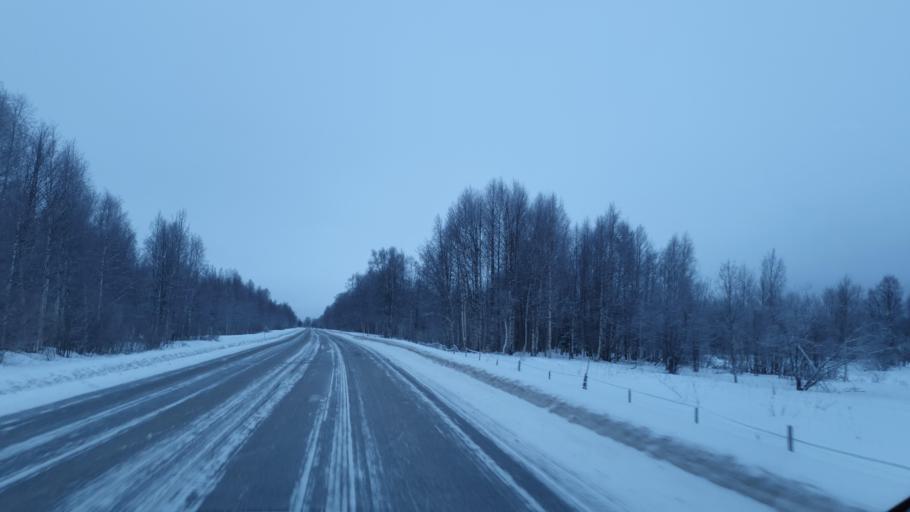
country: SE
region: Norrbotten
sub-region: Overtornea Kommun
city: OEvertornea
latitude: 66.4074
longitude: 23.6728
